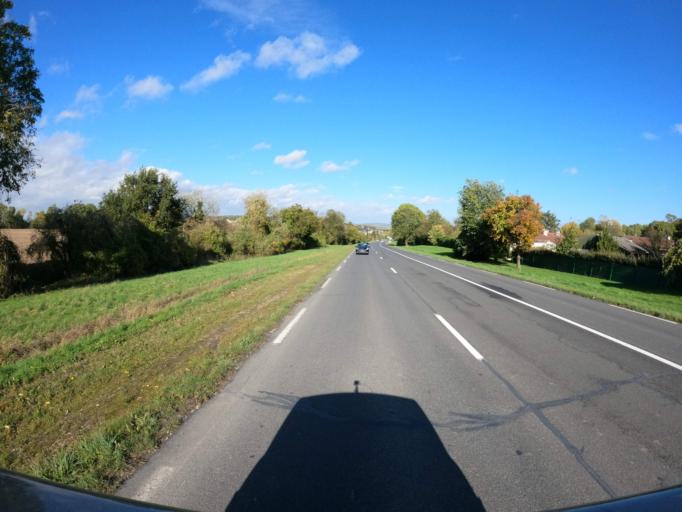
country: FR
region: Ile-de-France
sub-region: Departement de Seine-et-Marne
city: Coupvray
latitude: 48.8912
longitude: 2.8080
